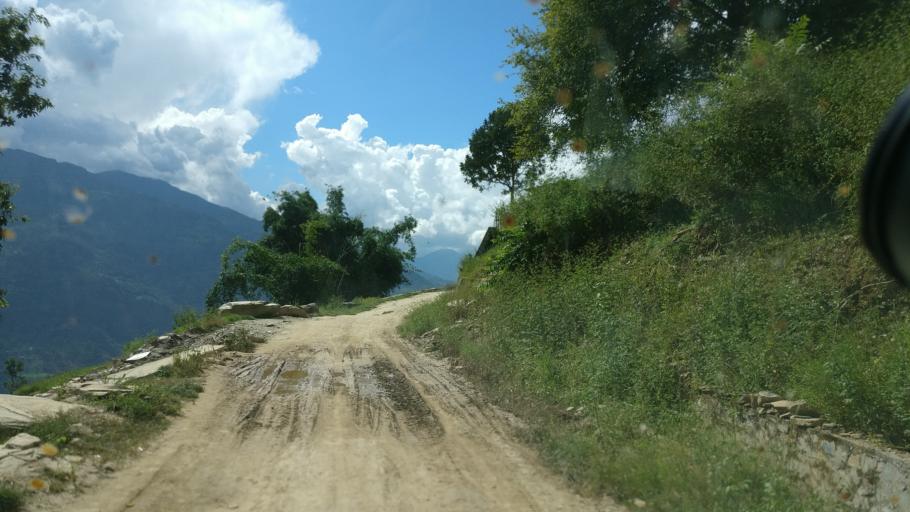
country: NP
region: Western Region
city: Baglung
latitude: 28.2604
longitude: 83.6458
